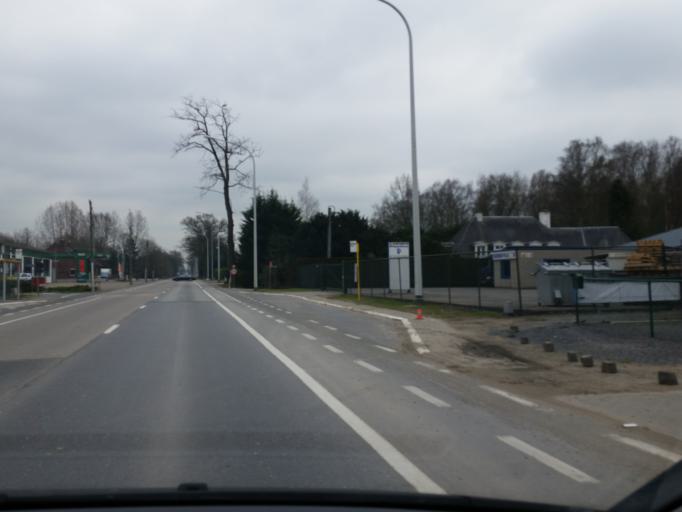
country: BE
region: Flanders
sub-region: Provincie Antwerpen
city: Bonheiden
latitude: 50.9913
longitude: 4.5371
